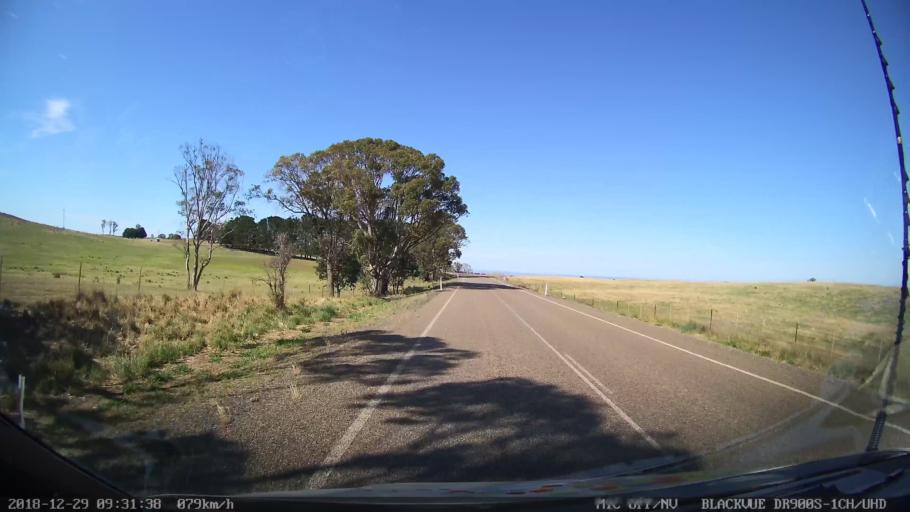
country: AU
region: New South Wales
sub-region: Upper Lachlan Shire
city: Crookwell
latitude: -34.6089
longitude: 149.3605
